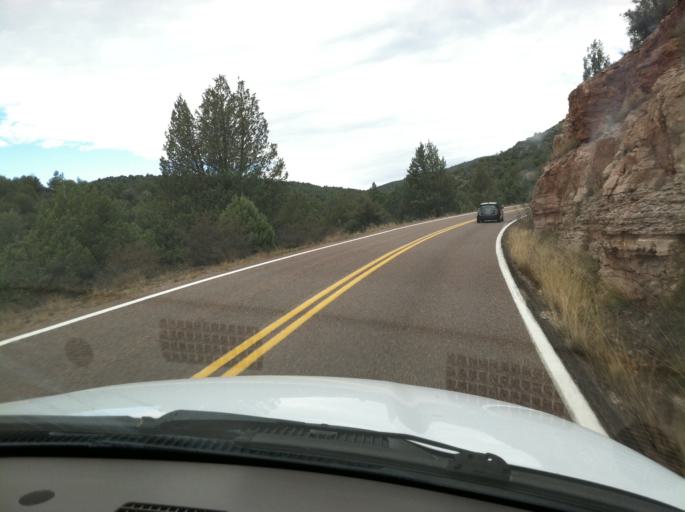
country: US
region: Arizona
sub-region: Gila County
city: Payson
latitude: 34.3159
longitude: -111.3734
